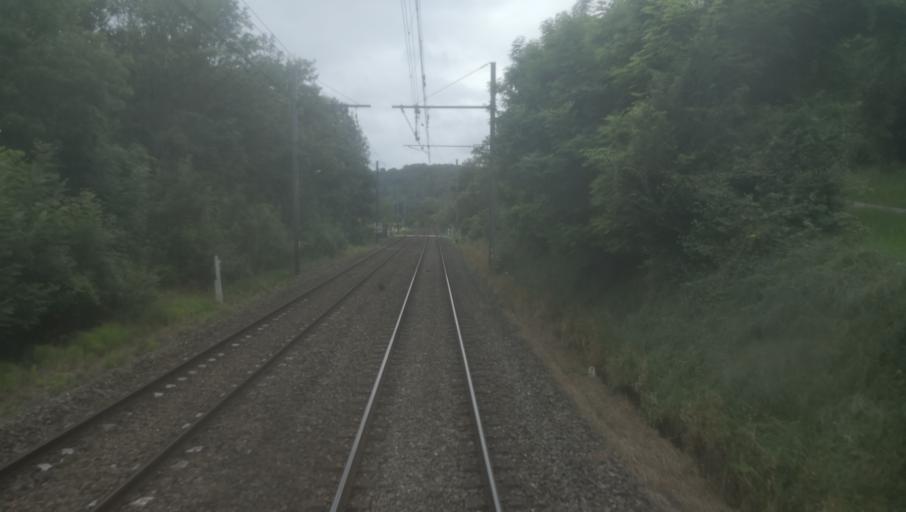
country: FR
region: Midi-Pyrenees
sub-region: Departement du Tarn-et-Garonne
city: Saint-Nicolas-de-la-Grave
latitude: 44.0916
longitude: 1.0092
